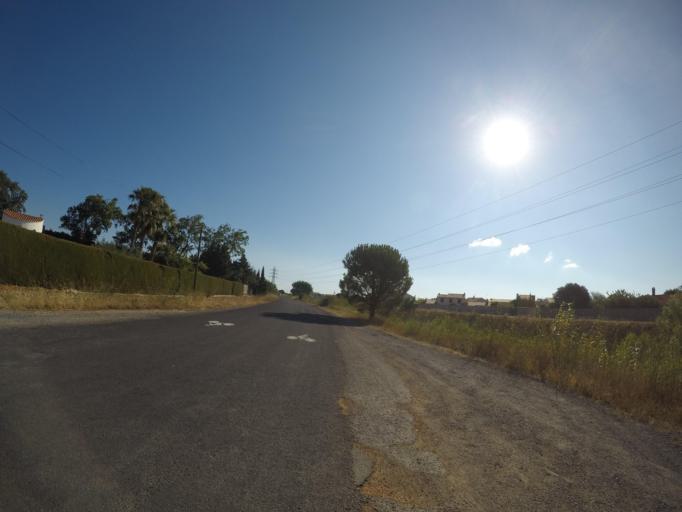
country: FR
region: Languedoc-Roussillon
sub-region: Departement des Pyrenees-Orientales
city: Pezilla-la-Riviere
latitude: 42.6792
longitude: 2.7743
